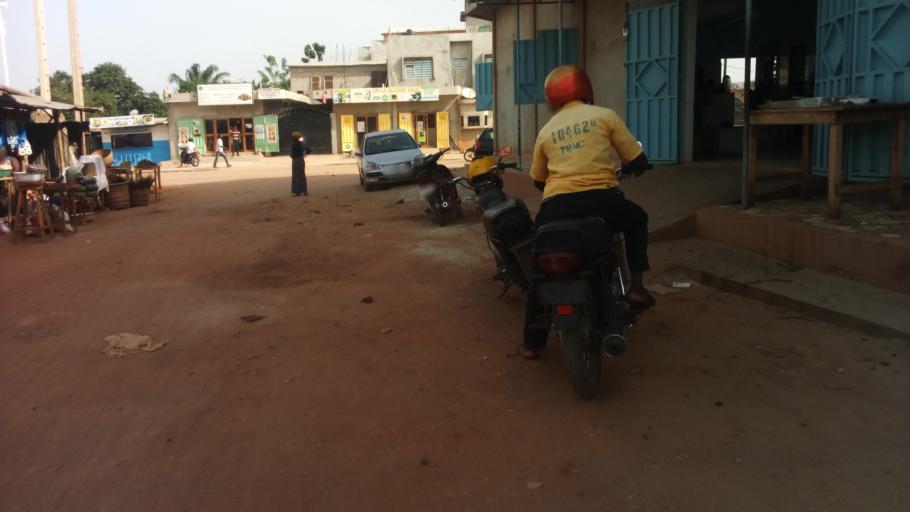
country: BJ
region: Atlantique
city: Abomey-Calavi
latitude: 6.4286
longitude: 2.3279
